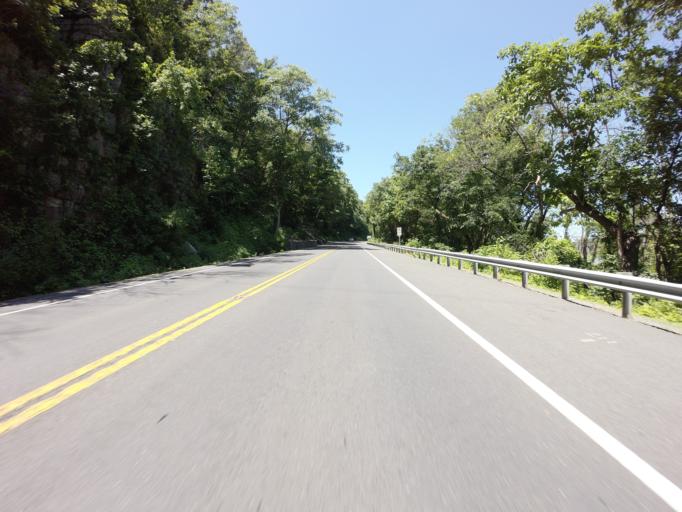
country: US
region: West Virginia
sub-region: Jefferson County
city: Bolivar
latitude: 39.3210
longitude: -77.7226
